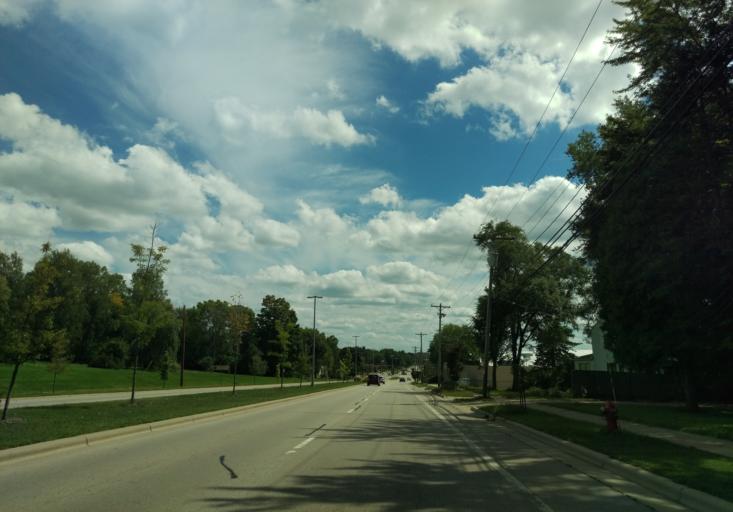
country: US
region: Wisconsin
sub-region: Dane County
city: Maple Bluff
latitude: 43.1354
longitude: -89.3752
